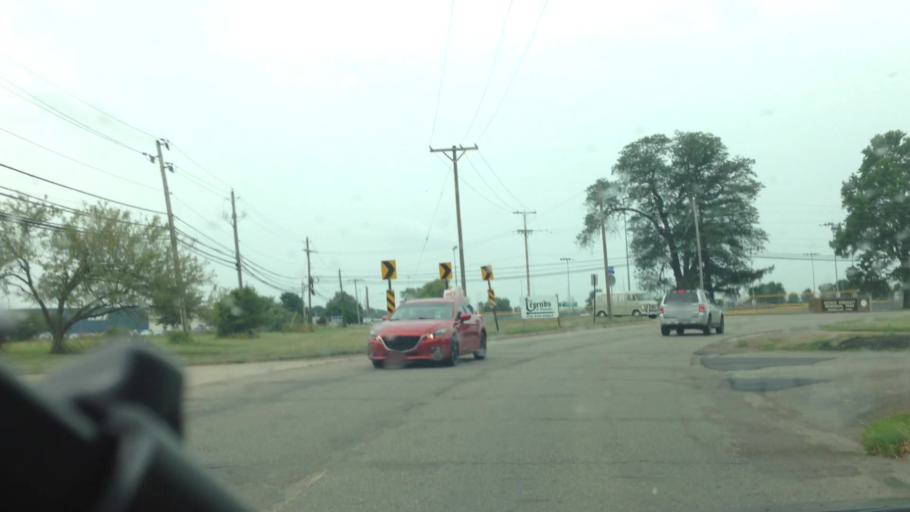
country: US
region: Ohio
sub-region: Stark County
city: Massillon
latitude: 40.7692
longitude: -81.5157
